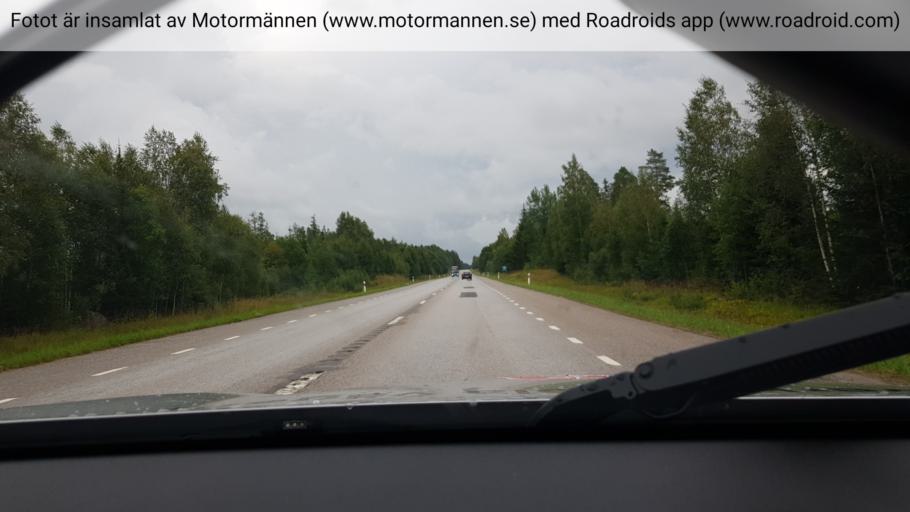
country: SE
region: Uppsala
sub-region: Alvkarleby Kommun
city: AElvkarleby
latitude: 60.5511
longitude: 17.5009
